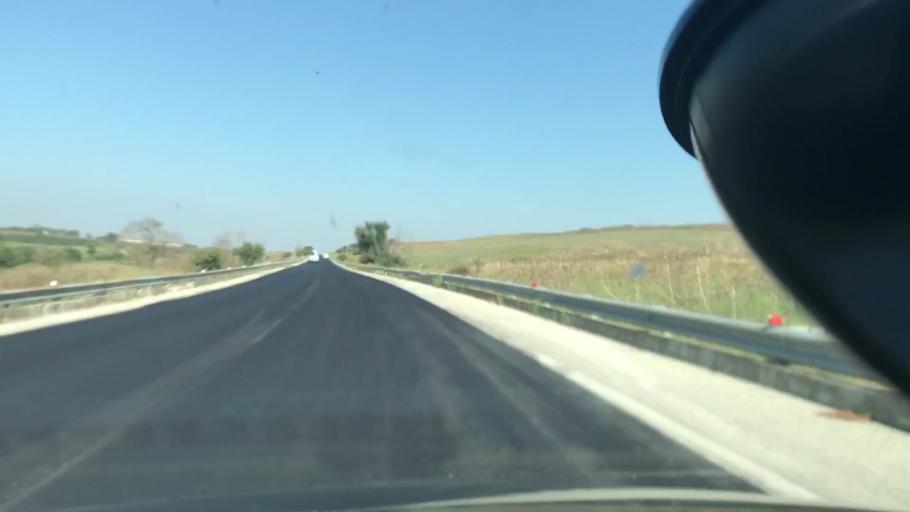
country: IT
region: Apulia
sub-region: Provincia di Barletta - Andria - Trani
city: Spinazzola
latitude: 40.9021
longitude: 16.1190
